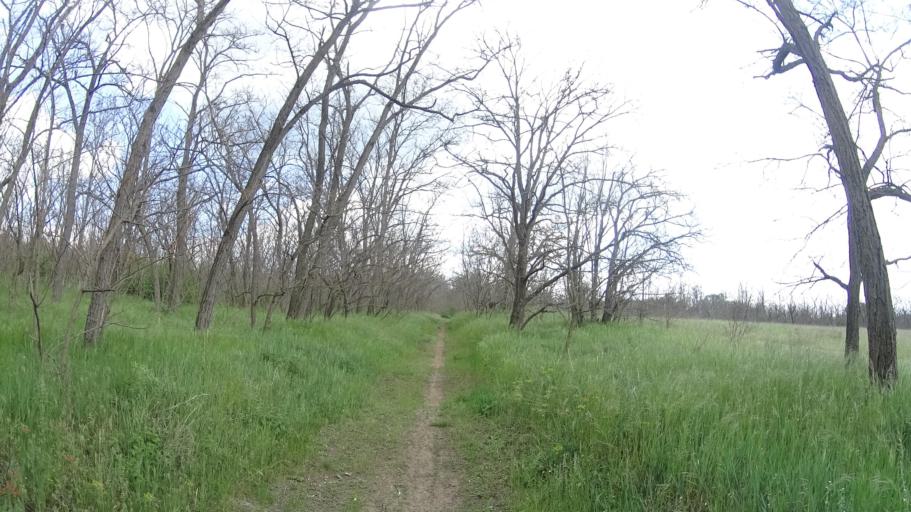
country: HU
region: Komarom-Esztergom
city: Dorog
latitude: 47.7151
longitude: 18.7574
